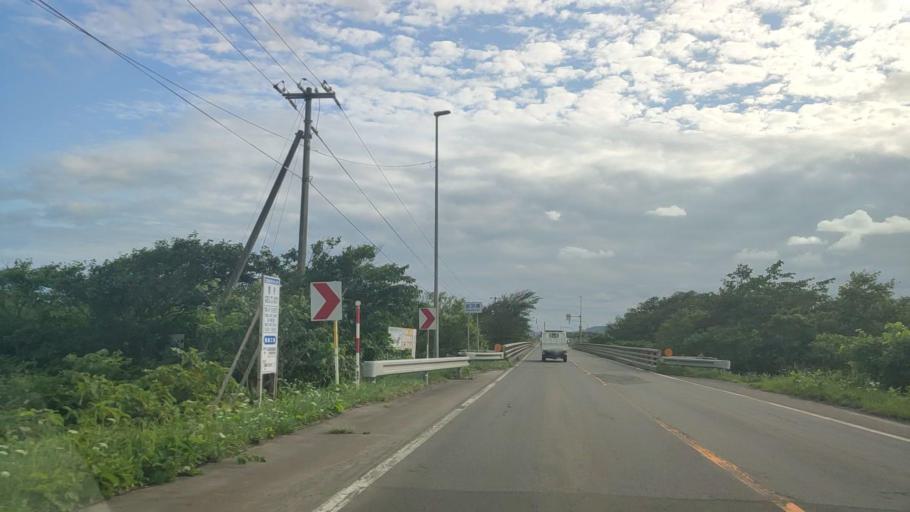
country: JP
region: Hokkaido
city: Niseko Town
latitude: 42.4895
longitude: 140.3572
